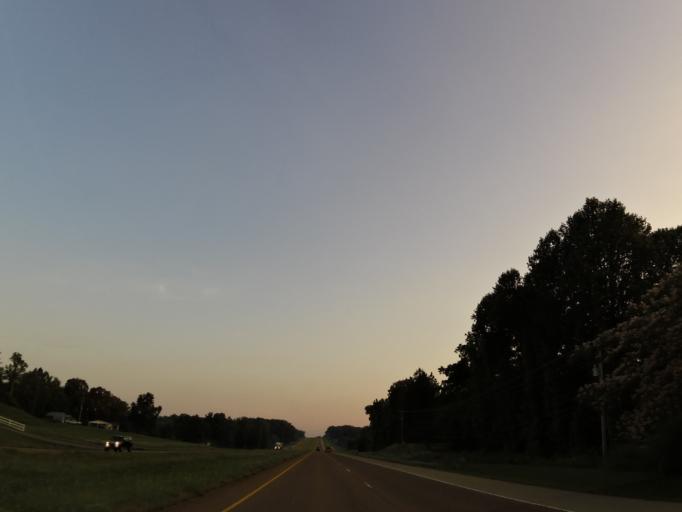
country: US
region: Tennessee
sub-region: Henry County
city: Paris
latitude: 36.2493
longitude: -88.3525
